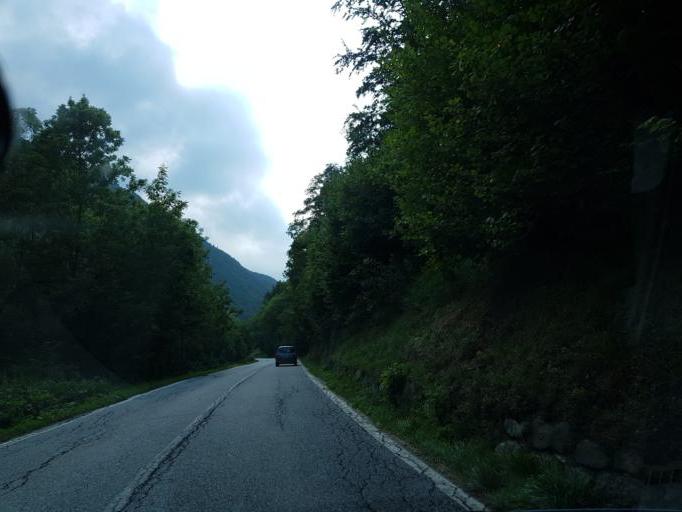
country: IT
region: Piedmont
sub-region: Provincia di Cuneo
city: Sampeyre
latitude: 44.5794
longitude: 7.1623
